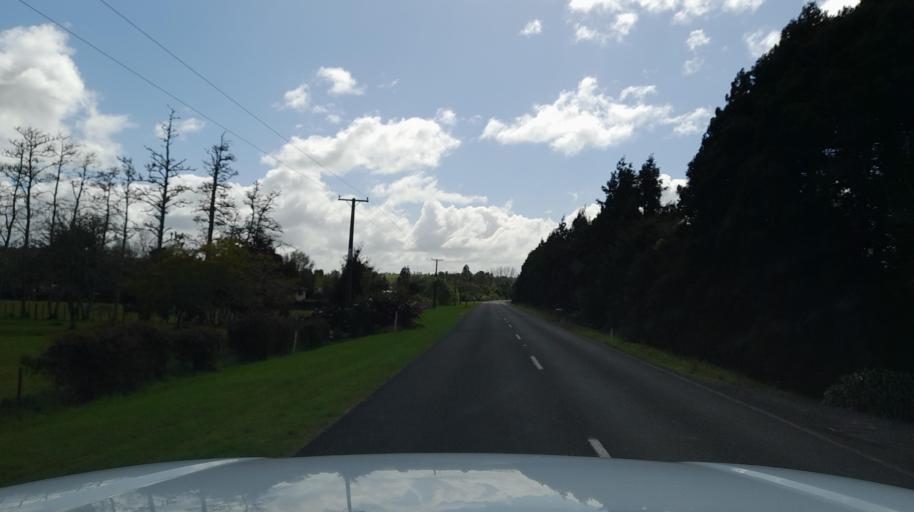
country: NZ
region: Northland
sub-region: Far North District
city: Kerikeri
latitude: -35.2349
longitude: 173.8779
